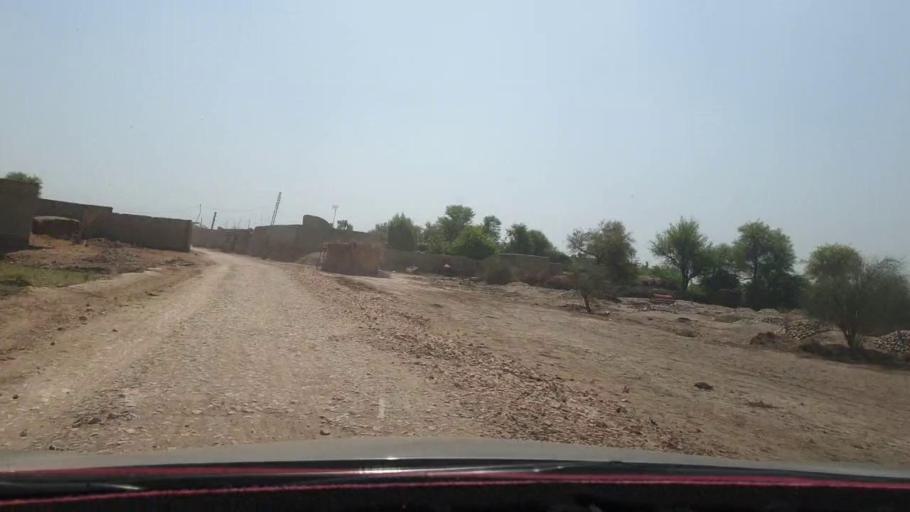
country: PK
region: Sindh
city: Warah
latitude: 27.4854
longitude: 67.8233
